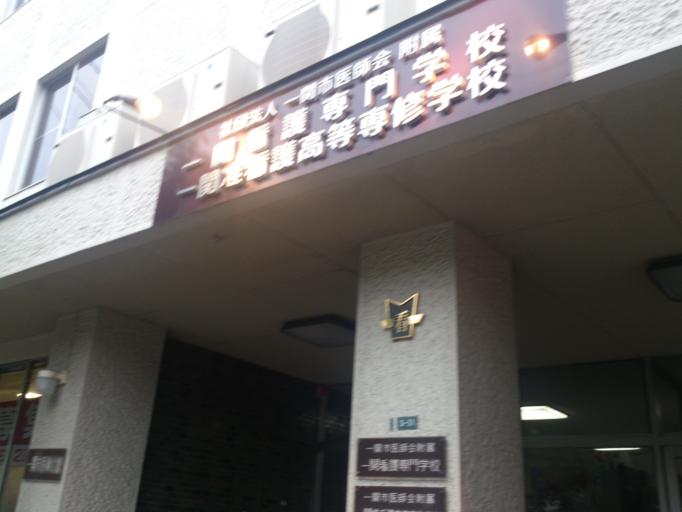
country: JP
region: Iwate
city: Ichinoseki
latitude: 38.9302
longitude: 141.1342
